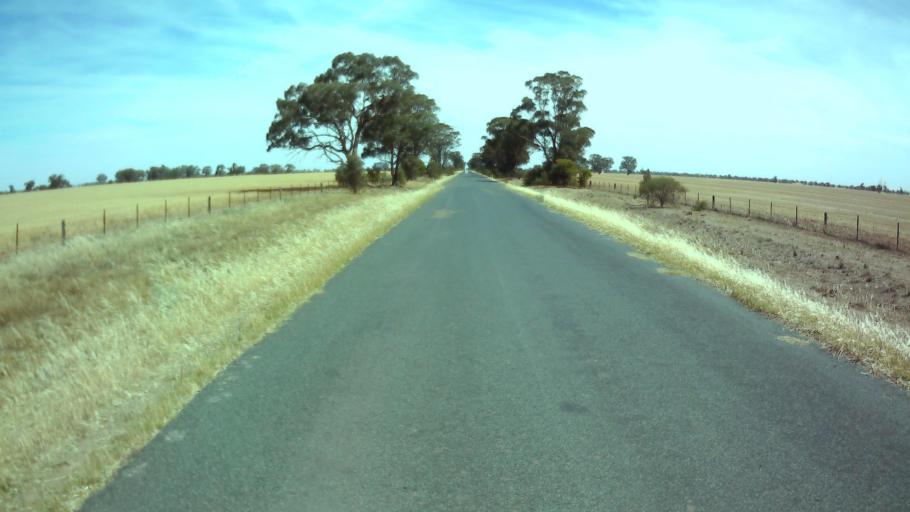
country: AU
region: New South Wales
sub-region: Weddin
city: Grenfell
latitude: -33.9622
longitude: 147.7817
